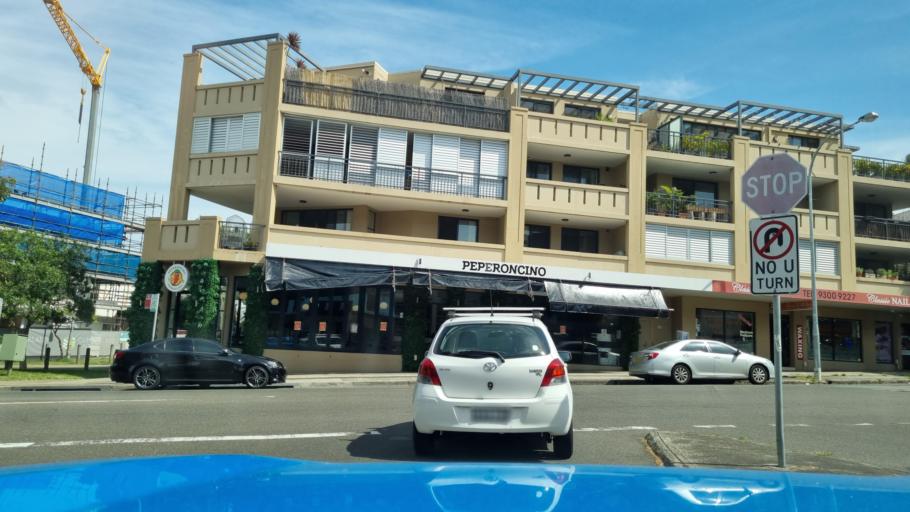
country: AU
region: New South Wales
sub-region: Waverley
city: Bondi Beach
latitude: -33.8889
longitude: 151.2705
